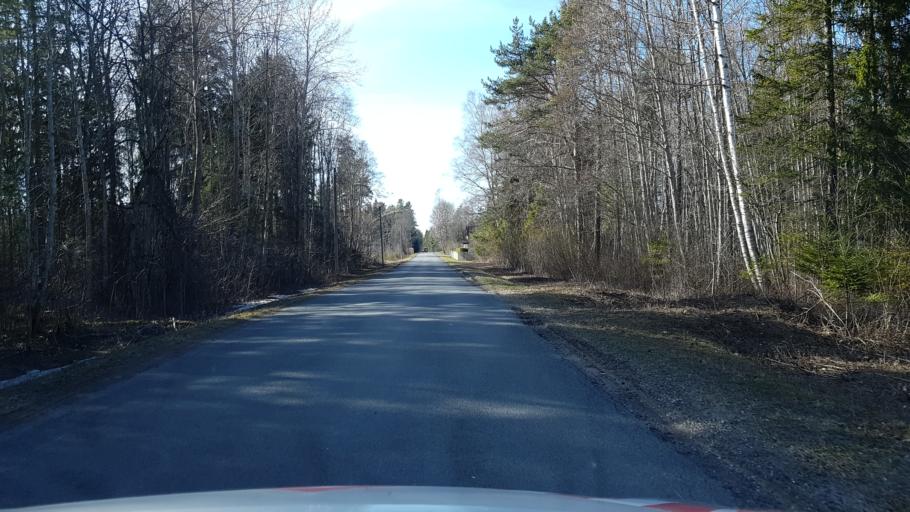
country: EE
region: Harju
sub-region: Nissi vald
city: Riisipere
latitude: 59.0972
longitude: 24.3373
